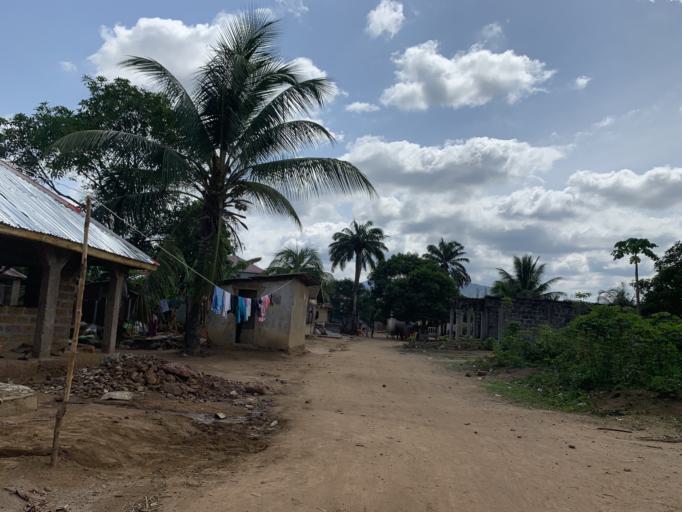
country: SL
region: Western Area
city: Waterloo
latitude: 8.3374
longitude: -13.0480
